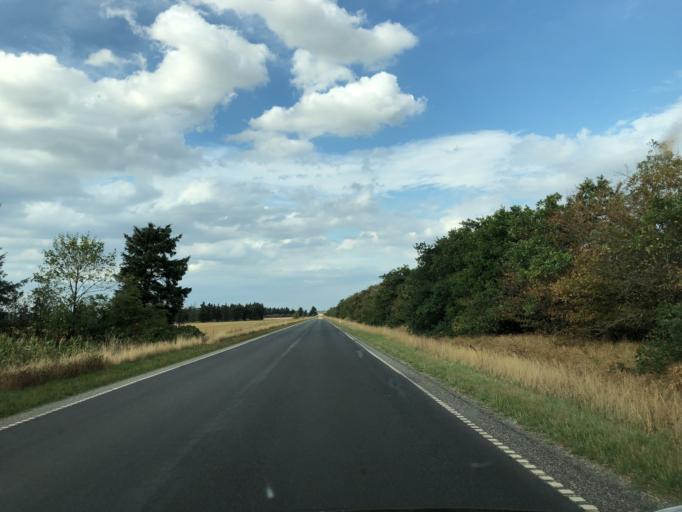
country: DK
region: Central Jutland
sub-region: Holstebro Kommune
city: Holstebro
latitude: 56.3856
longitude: 8.4525
